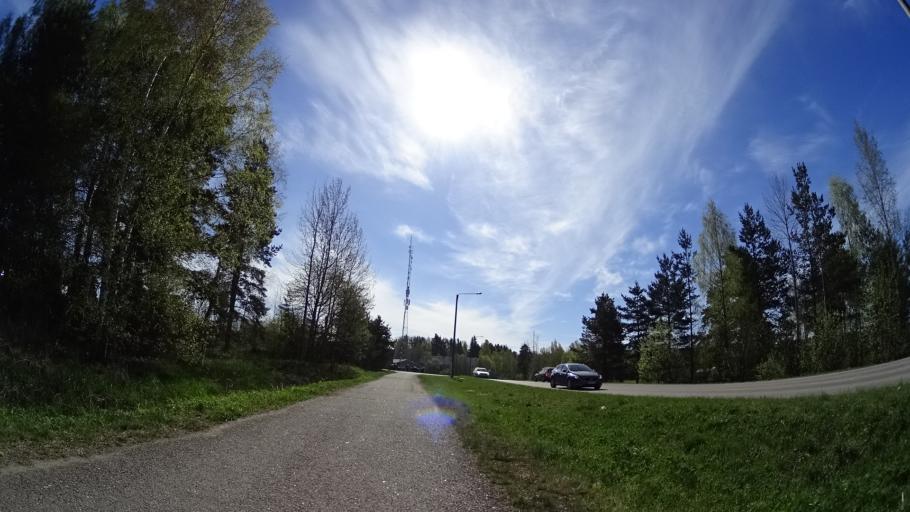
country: FI
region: Uusimaa
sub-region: Helsinki
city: Nurmijaervi
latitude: 60.4574
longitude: 24.8203
